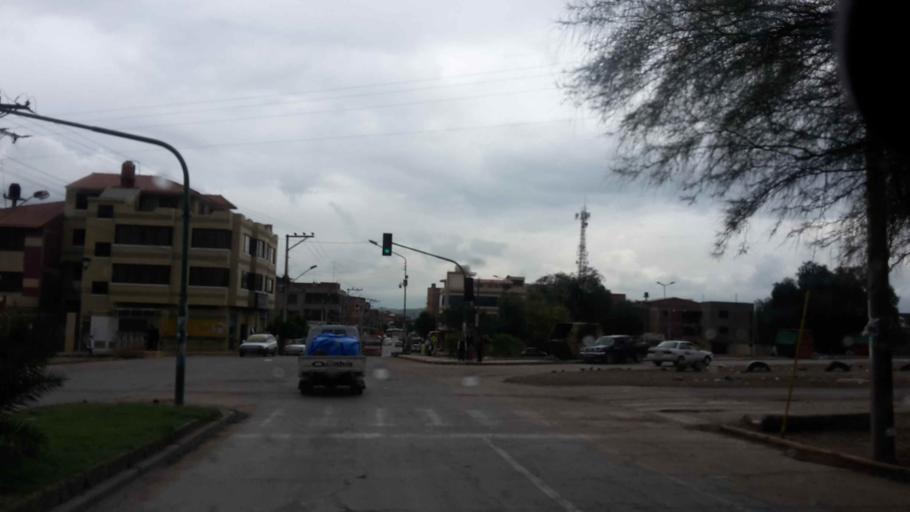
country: BO
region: Cochabamba
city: Cochabamba
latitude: -17.4292
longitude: -66.1552
